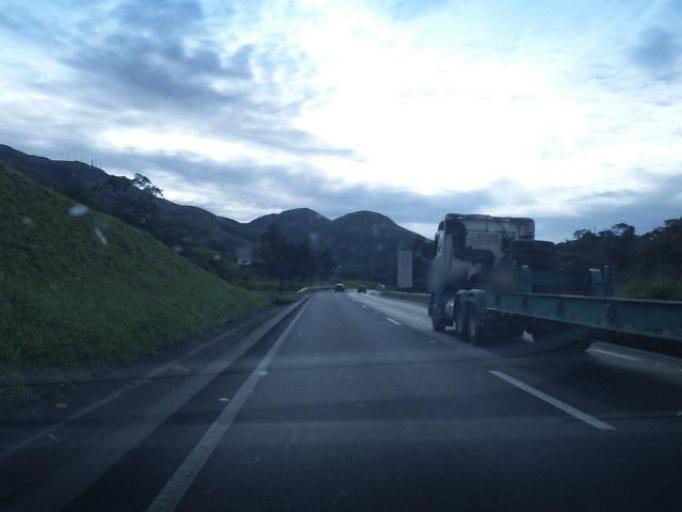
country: BR
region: Parana
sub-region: Campina Grande Do Sul
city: Campina Grande do Sul
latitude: -25.1090
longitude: -48.7978
